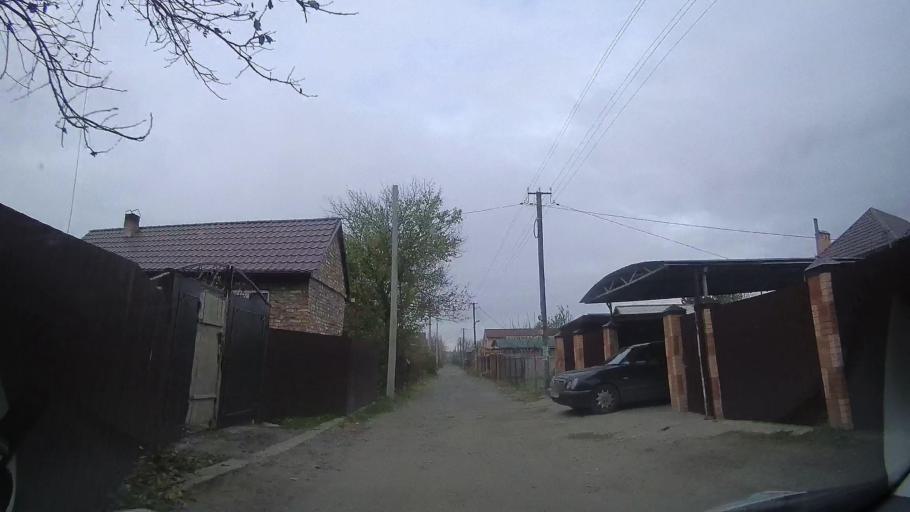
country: RU
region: Rostov
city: Bataysk
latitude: 47.0832
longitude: 39.7594
